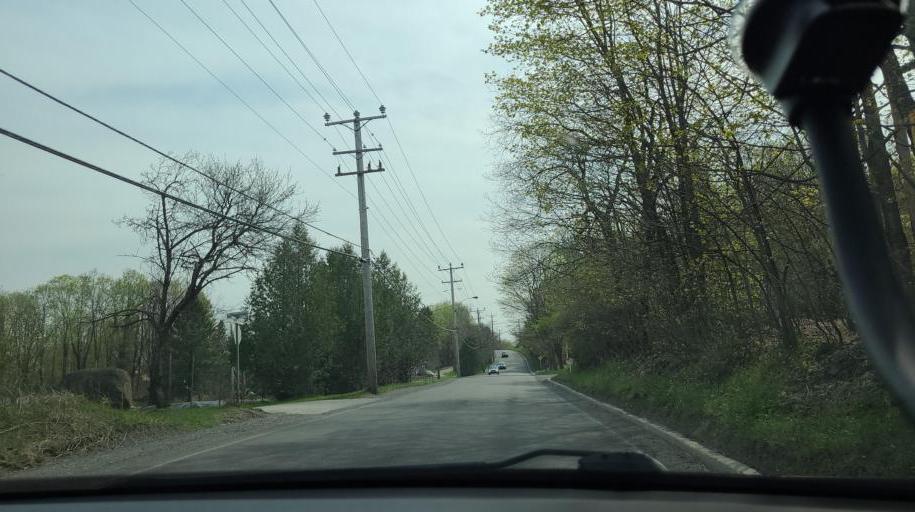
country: CA
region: Quebec
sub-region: Laurentides
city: Prevost
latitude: 45.8799
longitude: -74.0625
